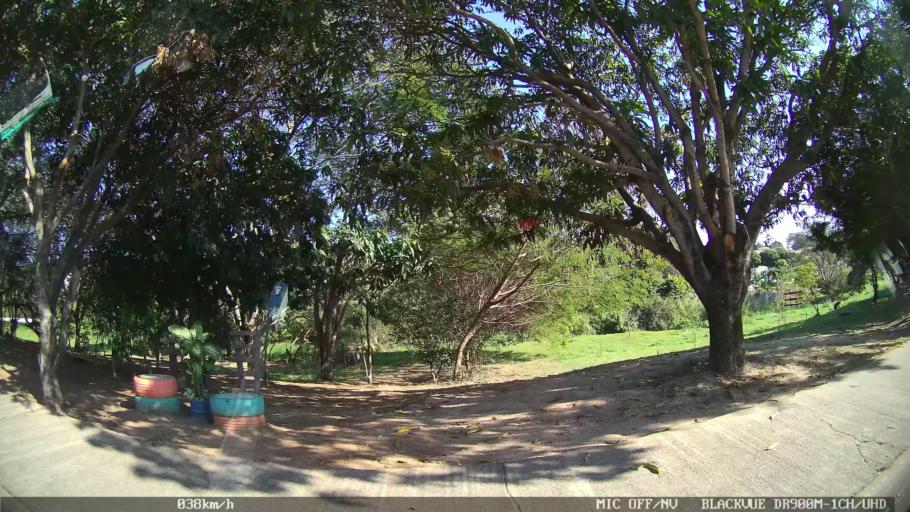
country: BR
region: Sao Paulo
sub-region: Campinas
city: Campinas
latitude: -22.9419
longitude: -47.1228
